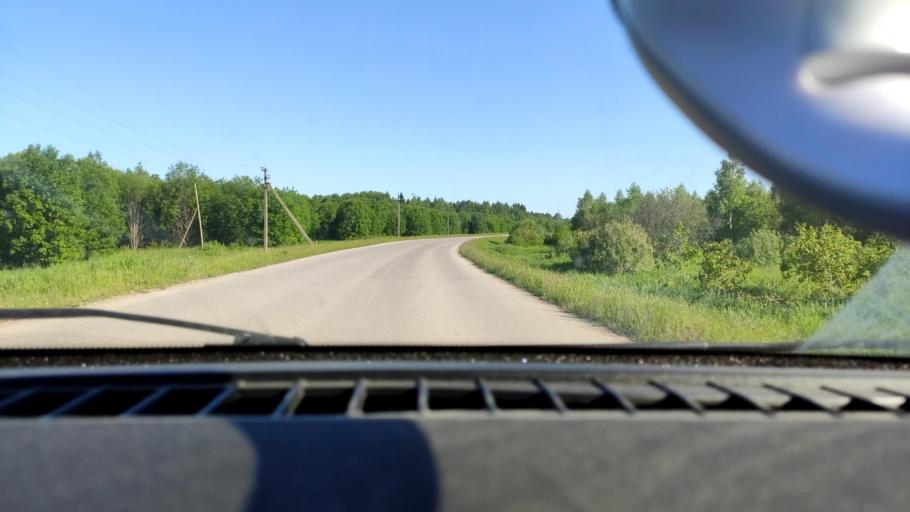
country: RU
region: Perm
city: Polazna
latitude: 58.1992
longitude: 56.5326
